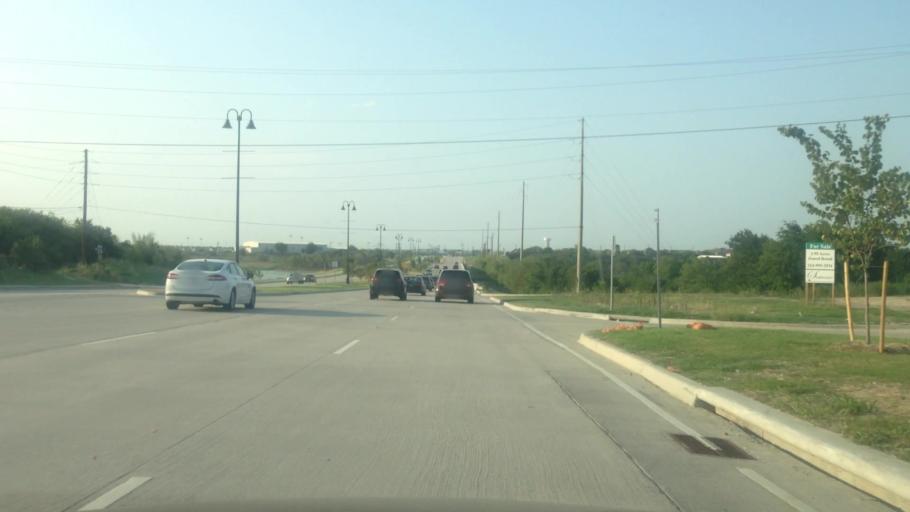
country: US
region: Texas
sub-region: Denton County
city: The Colony
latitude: 33.1057
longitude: -96.8917
